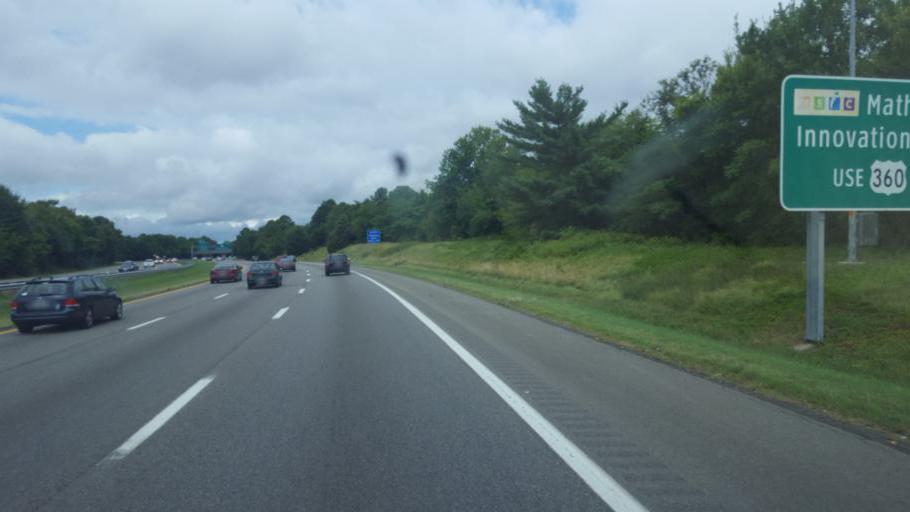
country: US
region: Virginia
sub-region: Henrico County
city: East Highland Park
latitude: 37.5536
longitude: -77.4025
